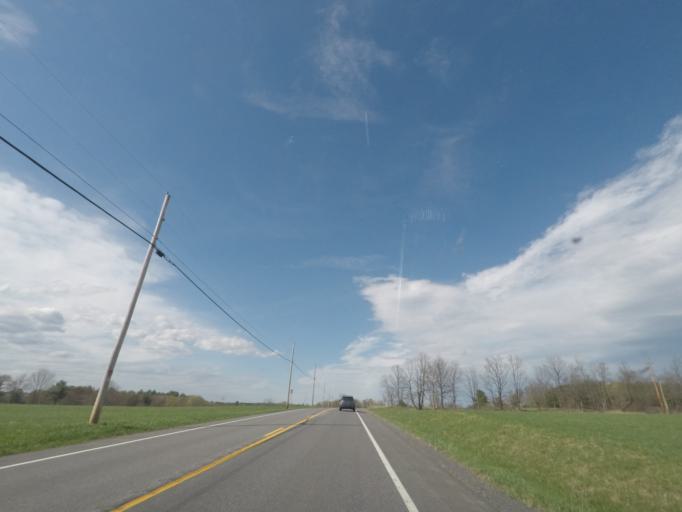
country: US
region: New York
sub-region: Greene County
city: Cairo
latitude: 42.4593
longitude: -74.0050
